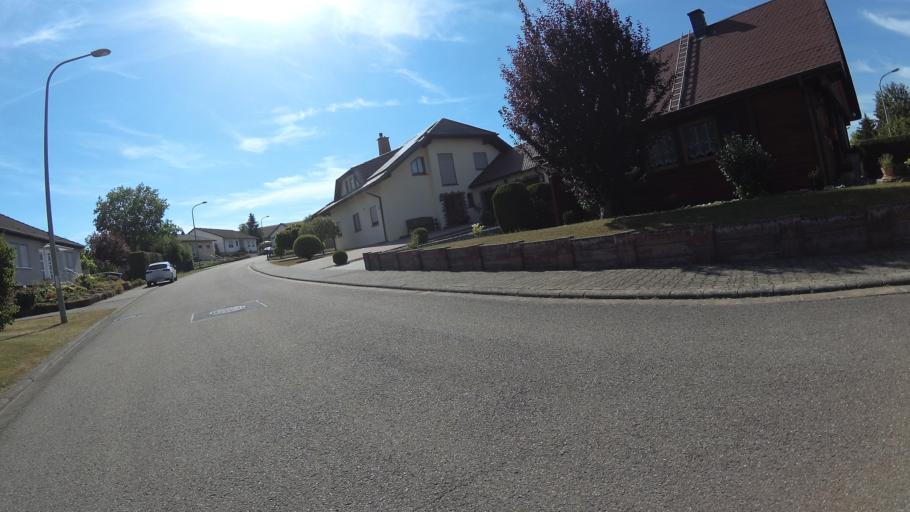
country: DE
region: Saarland
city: Gersheim
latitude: 49.1418
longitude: 7.2741
